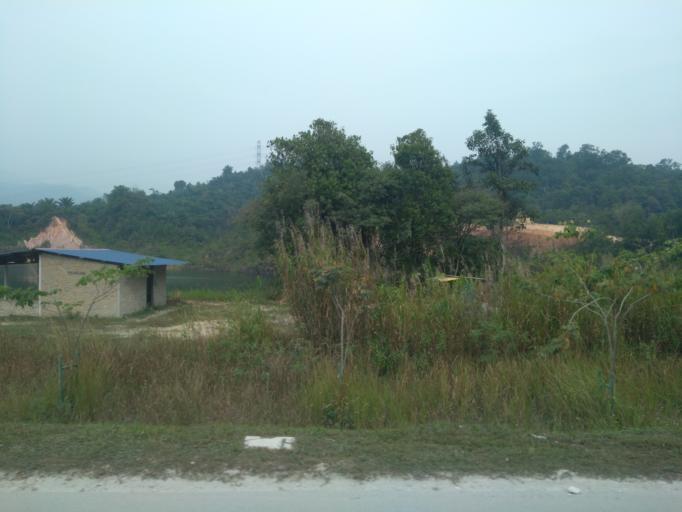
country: MY
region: Perak
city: Ipoh
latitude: 4.5506
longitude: 101.1635
